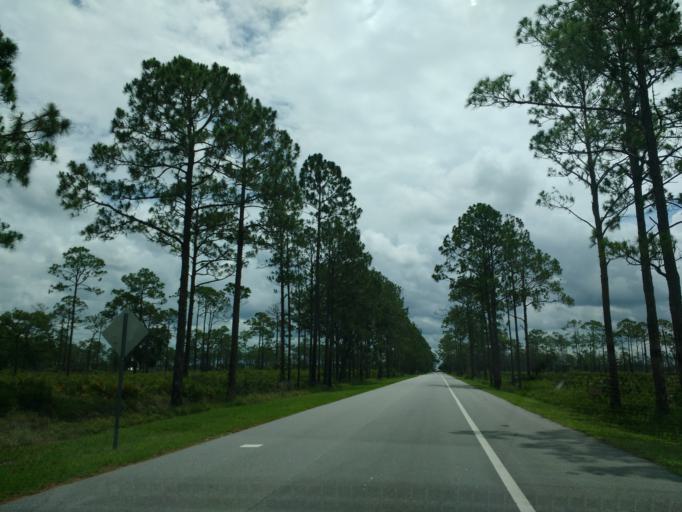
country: US
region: Florida
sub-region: Highlands County
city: Sebring
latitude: 27.4709
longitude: -81.5203
